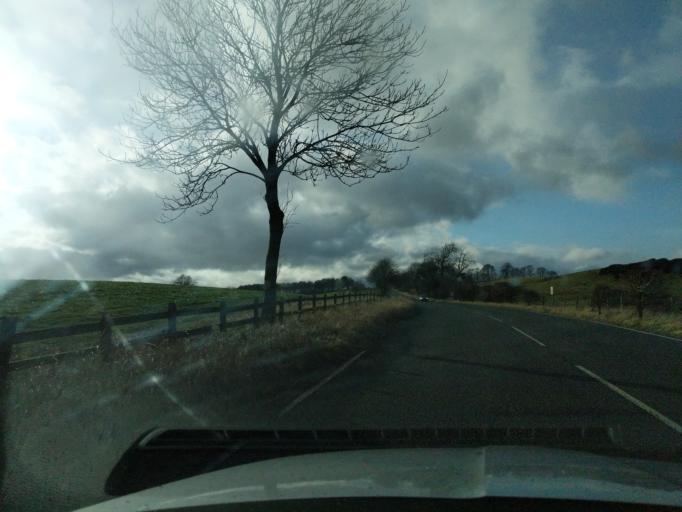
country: GB
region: England
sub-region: North Yorkshire
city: Catterick Garrison
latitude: 54.3473
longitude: -1.7592
